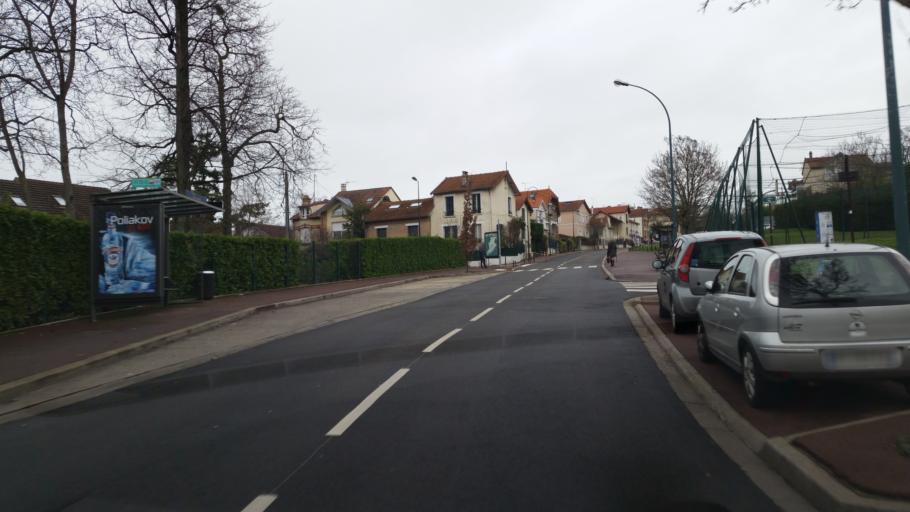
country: FR
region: Ile-de-France
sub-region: Departement des Hauts-de-Seine
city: Saint-Cloud
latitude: 48.8448
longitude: 2.1985
